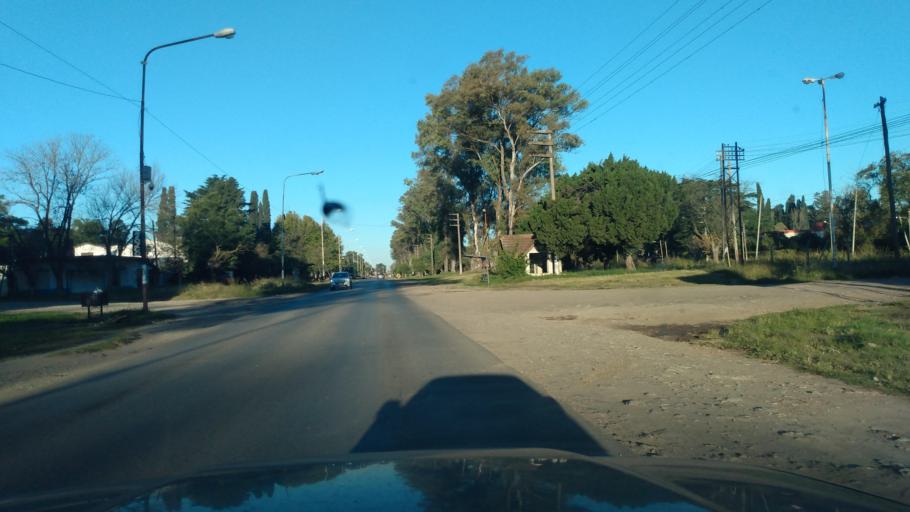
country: AR
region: Buenos Aires
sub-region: Partido de Merlo
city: Merlo
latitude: -34.6371
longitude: -58.8365
